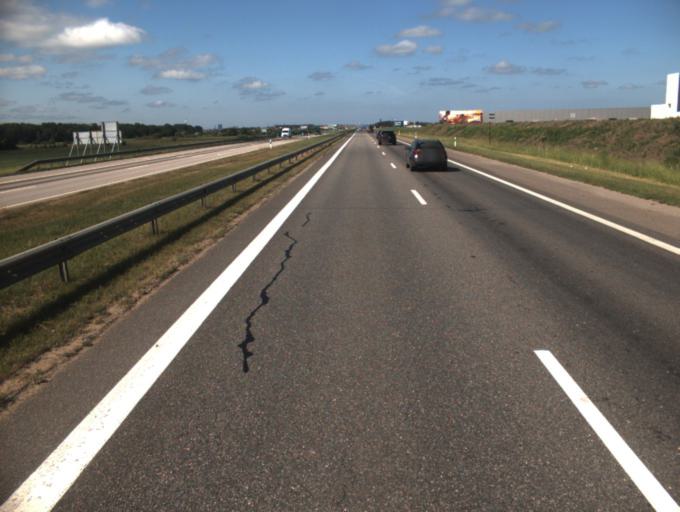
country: LT
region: Klaipedos apskritis
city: Gargzdai
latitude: 55.7180
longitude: 21.2868
